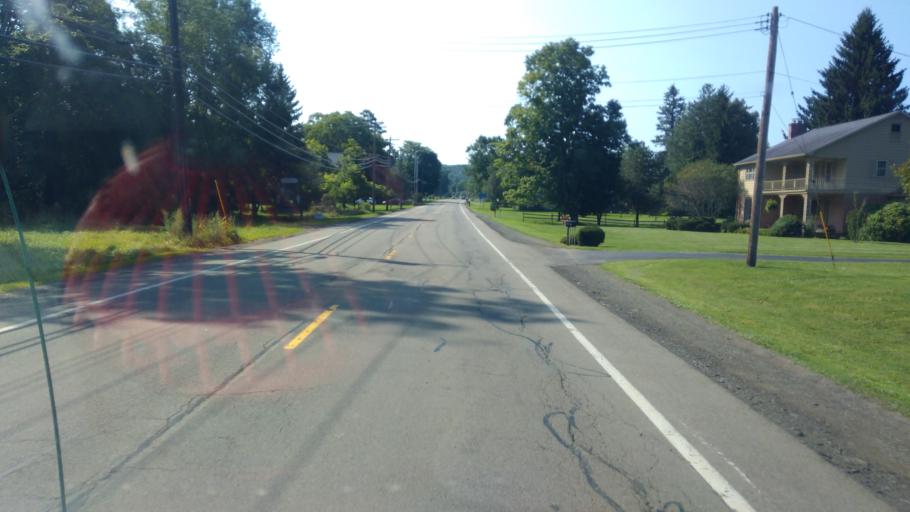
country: US
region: New York
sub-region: Allegany County
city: Cuba
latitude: 42.2074
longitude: -78.2750
